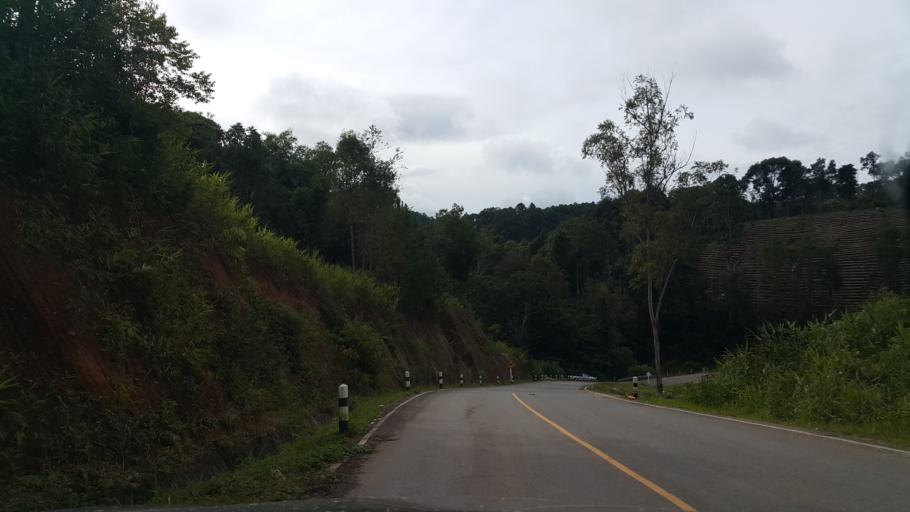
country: TH
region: Chiang Mai
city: Chaem Luang
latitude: 18.9363
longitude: 98.4536
